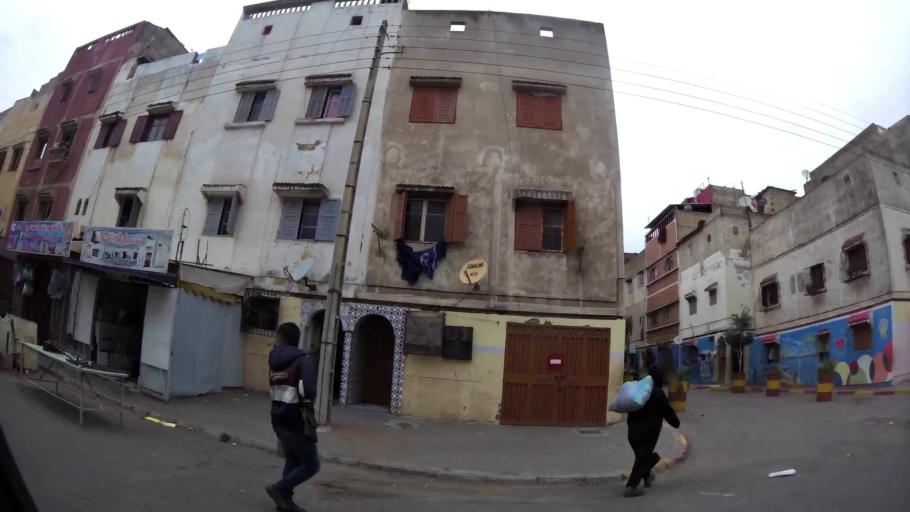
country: MA
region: Grand Casablanca
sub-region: Mediouna
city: Tit Mellil
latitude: 33.5636
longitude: -7.5427
